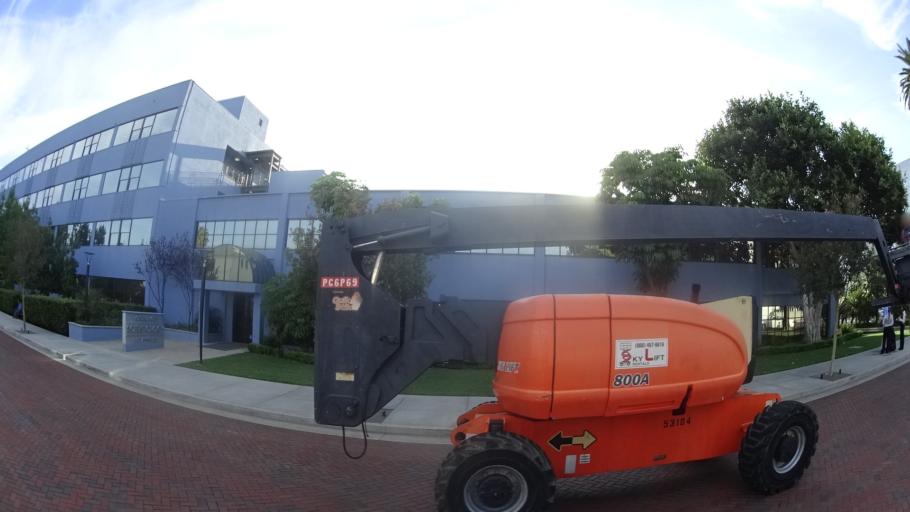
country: US
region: California
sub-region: Los Angeles County
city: Silver Lake
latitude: 34.0970
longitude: -118.2939
